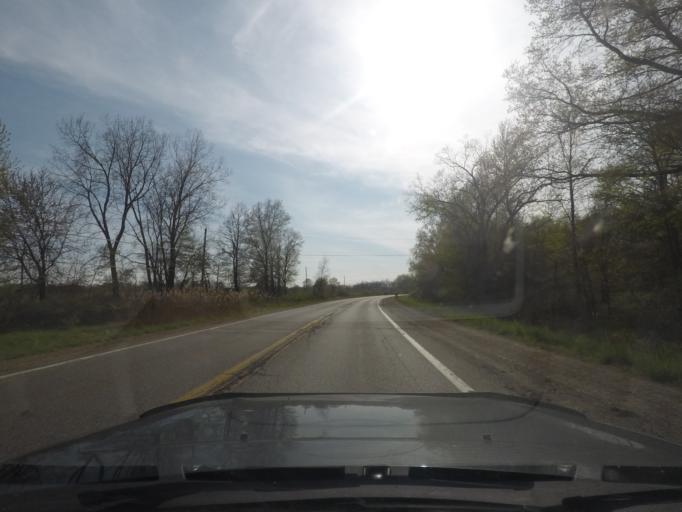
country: US
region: Michigan
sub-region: Berrien County
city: Buchanan
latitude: 41.7936
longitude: -86.4217
